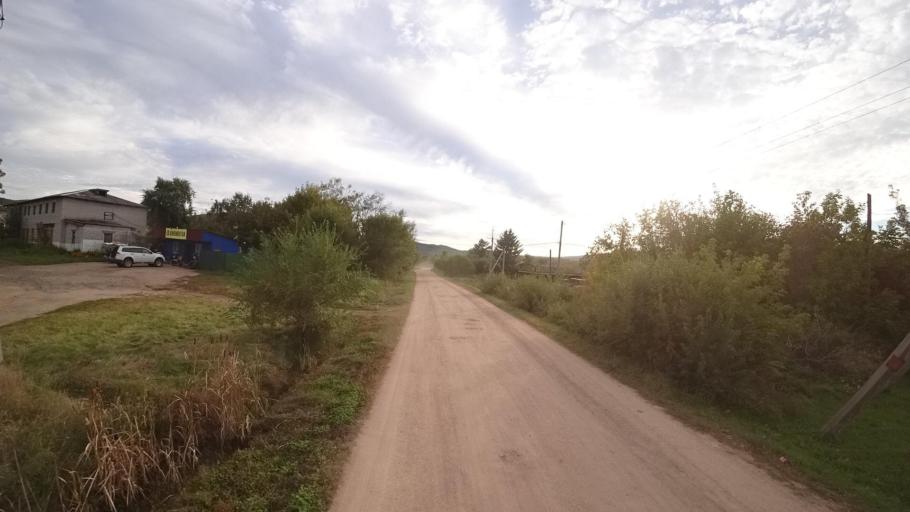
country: RU
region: Primorskiy
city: Yakovlevka
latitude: 44.4175
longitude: 133.4522
